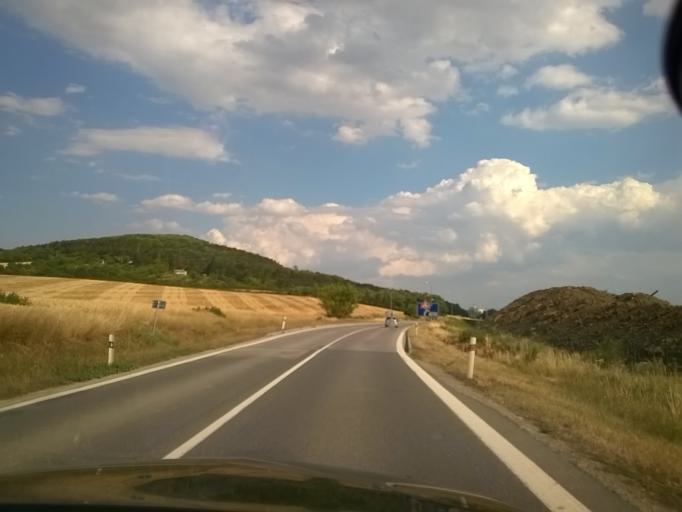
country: SK
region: Nitriansky
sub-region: Okres Nitra
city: Nitra
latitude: 48.3427
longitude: 18.0654
